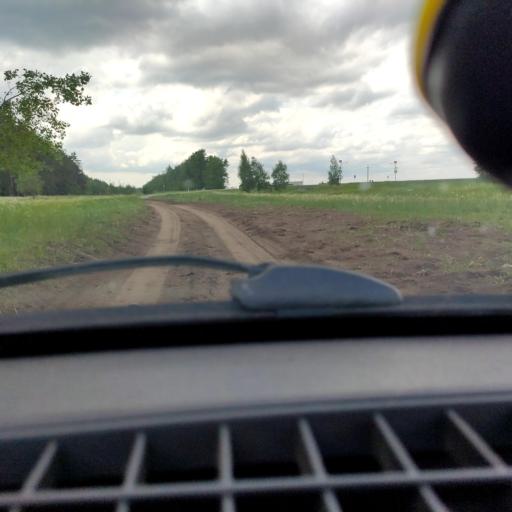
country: RU
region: Samara
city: Povolzhskiy
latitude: 53.6311
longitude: 49.6610
